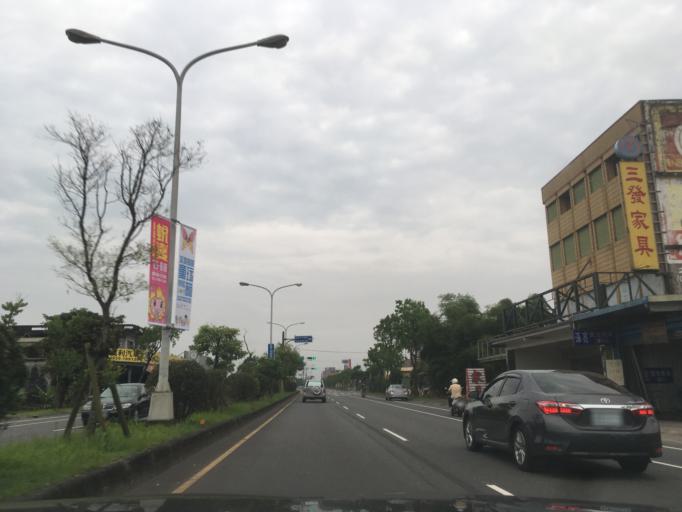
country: TW
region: Taiwan
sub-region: Yilan
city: Yilan
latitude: 24.7383
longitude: 121.7609
